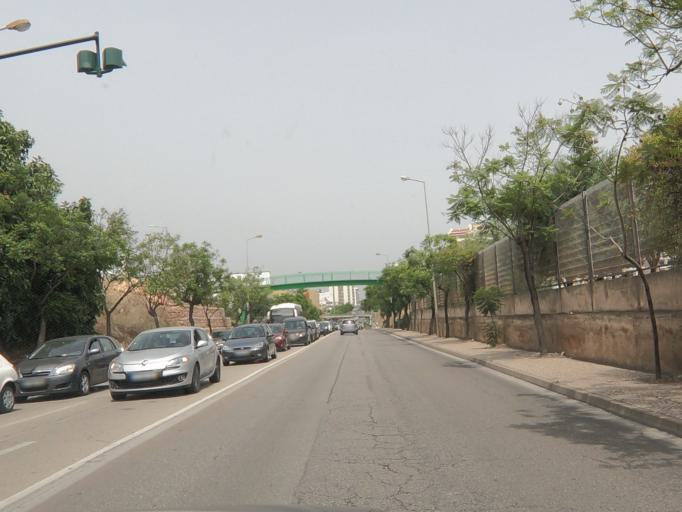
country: PT
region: Faro
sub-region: Portimao
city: Portimao
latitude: 37.1433
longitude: -8.5445
